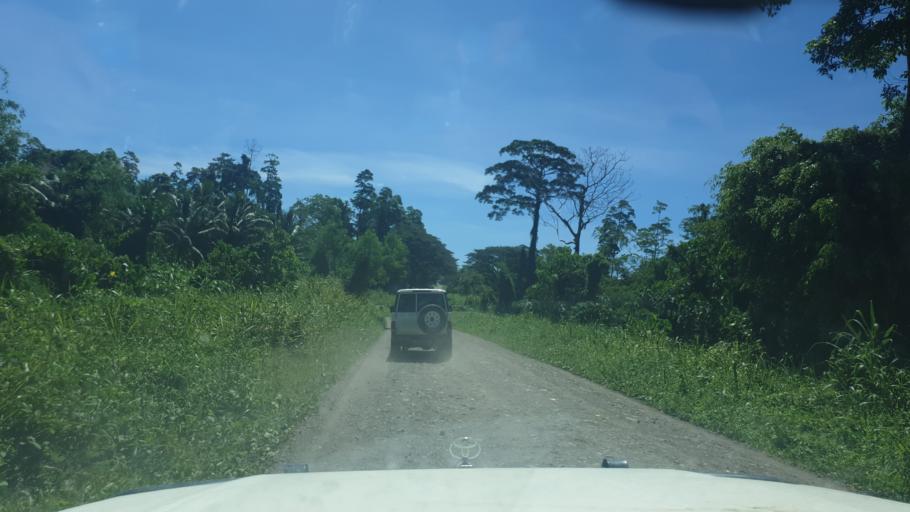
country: PG
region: Bougainville
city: Arawa
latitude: -5.8162
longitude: 155.1480
